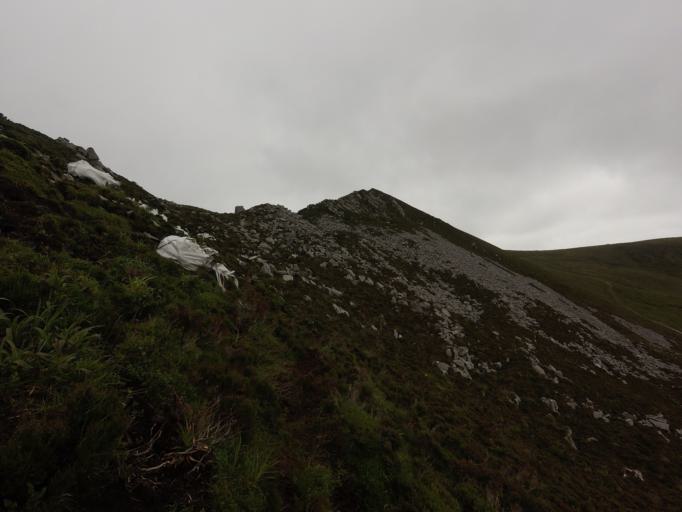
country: IE
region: Ulster
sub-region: County Donegal
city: Killybegs
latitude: 54.6433
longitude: -8.6859
